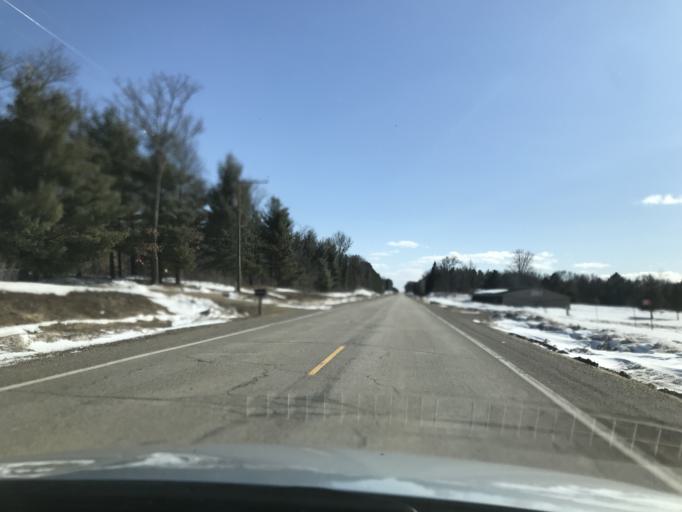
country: US
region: Wisconsin
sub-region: Marinette County
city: Peshtigo
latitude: 45.3179
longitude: -88.1023
